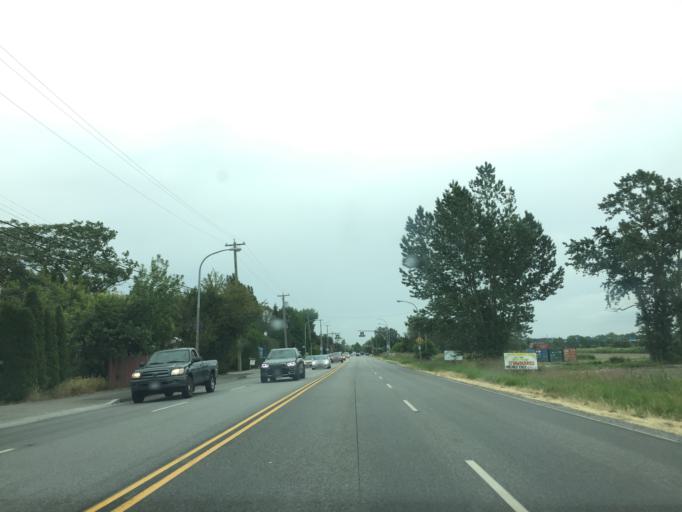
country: CA
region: British Columbia
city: Richmond
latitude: 49.1334
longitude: -123.1091
